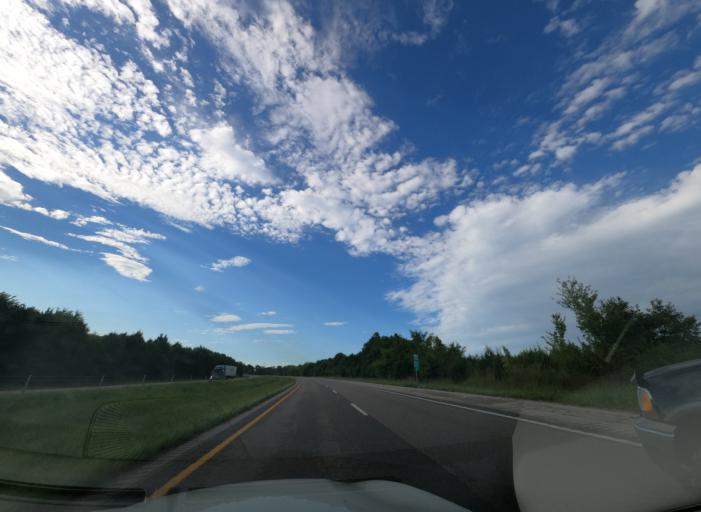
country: US
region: Missouri
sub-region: Jefferson County
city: Crystal City
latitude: 38.1265
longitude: -90.3120
